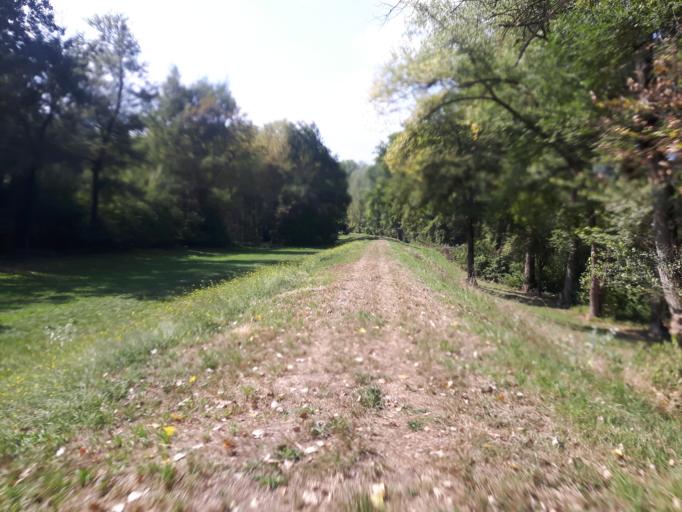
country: DE
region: Rheinland-Pfalz
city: Otterstadt
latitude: 49.3932
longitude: 8.4805
